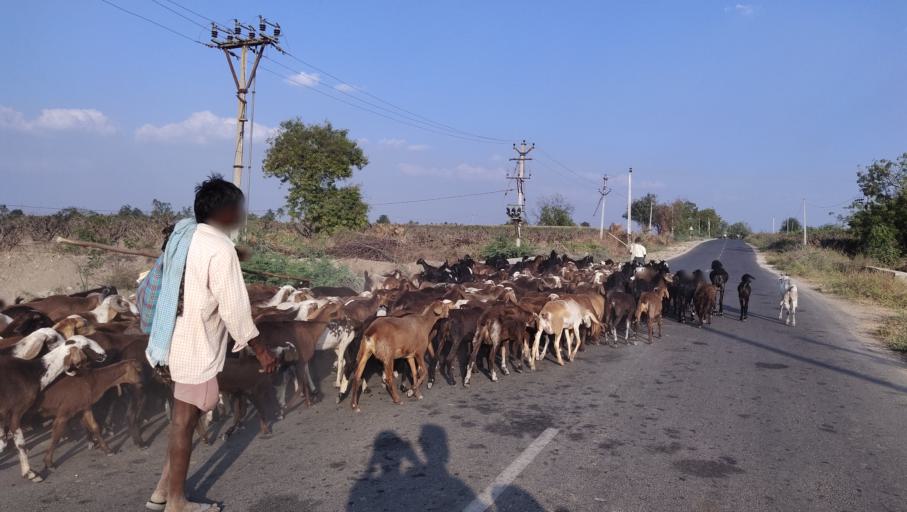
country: IN
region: Andhra Pradesh
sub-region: Anantapur
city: Tadpatri
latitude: 14.9507
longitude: 77.8885
